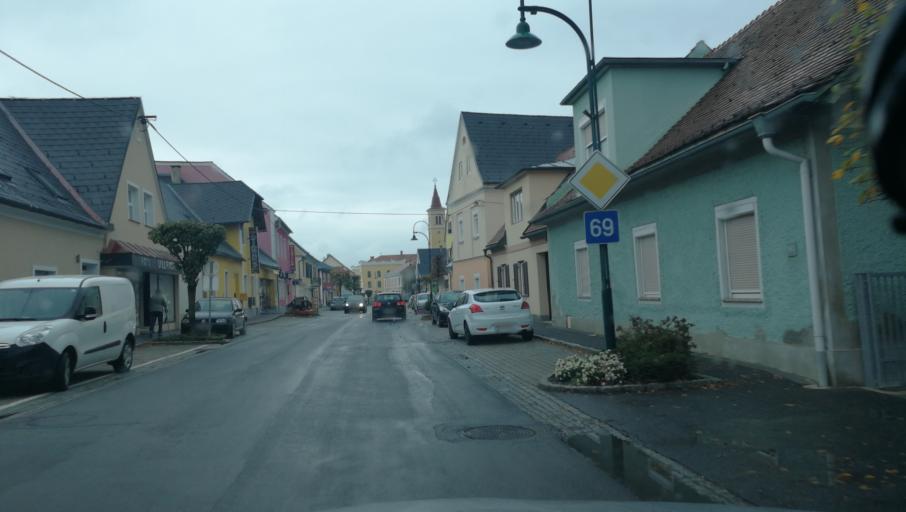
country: AT
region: Styria
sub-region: Politischer Bezirk Leibnitz
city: Strass in Steiermark
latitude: 46.7257
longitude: 15.6297
